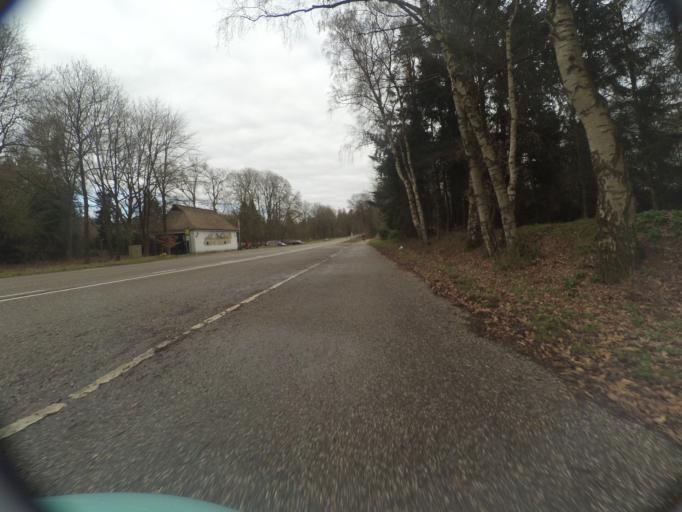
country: NL
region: Gelderland
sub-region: Gemeente Apeldoorn
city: Beekbergen
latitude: 52.1045
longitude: 5.9521
